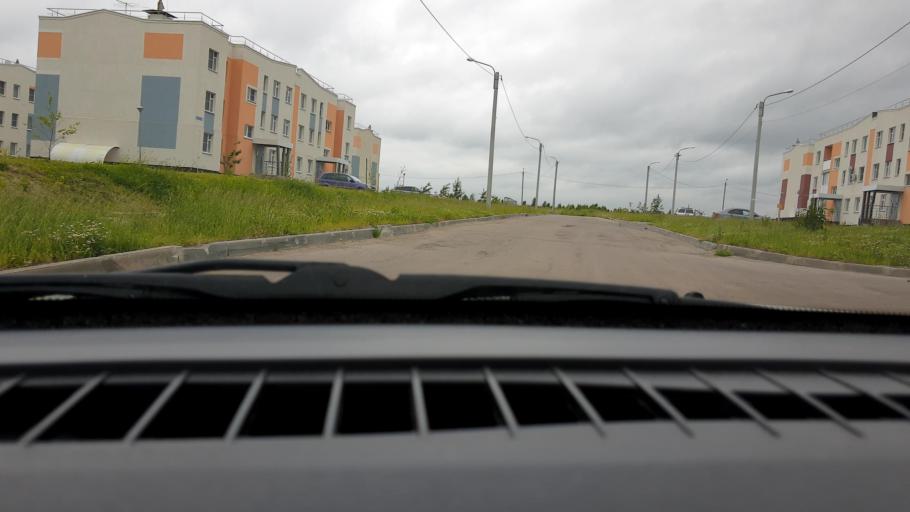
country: RU
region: Nizjnij Novgorod
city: Burevestnik
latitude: 56.1848
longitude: 43.8523
